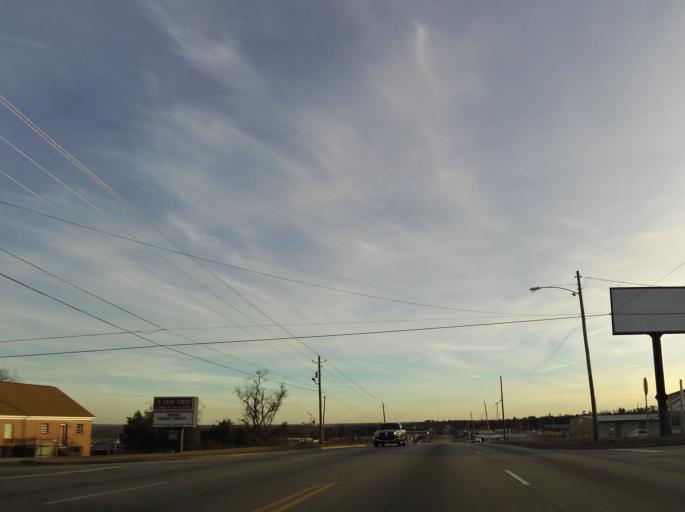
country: US
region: Georgia
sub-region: Bibb County
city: Macon
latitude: 32.8115
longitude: -83.6402
